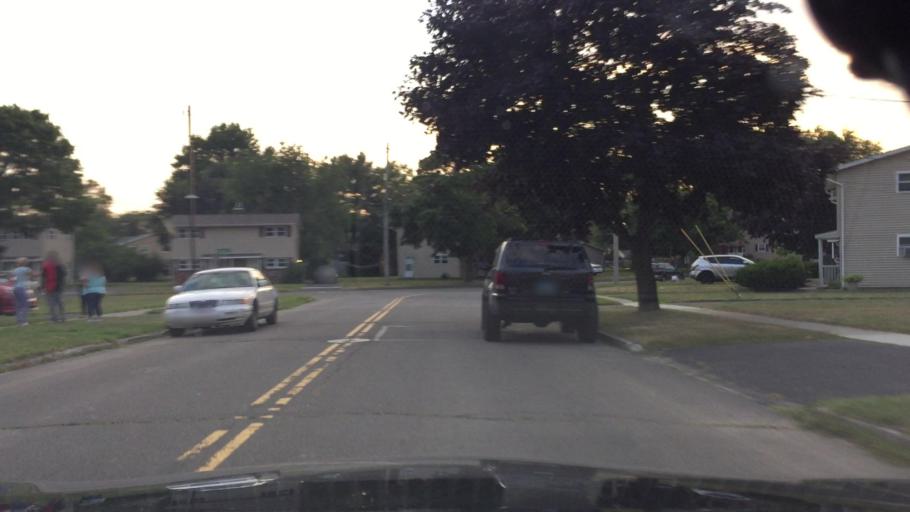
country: US
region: Connecticut
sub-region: Fairfield County
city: Stratford
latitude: 41.1751
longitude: -73.1318
